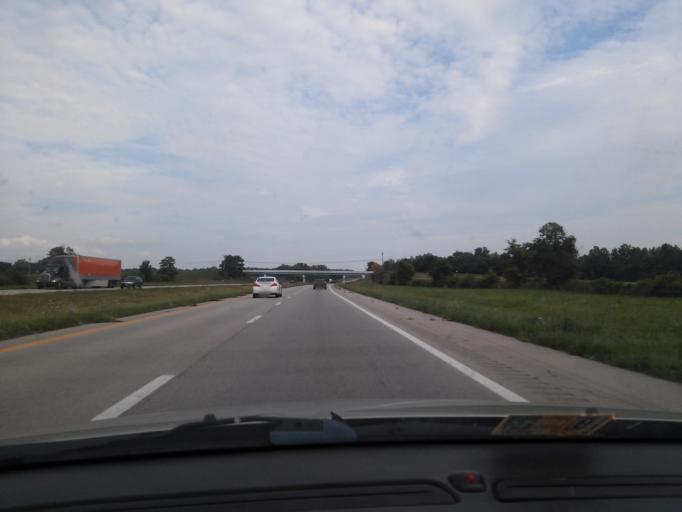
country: US
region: Ohio
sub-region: Ross County
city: Frankfort
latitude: 39.4207
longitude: -83.1474
